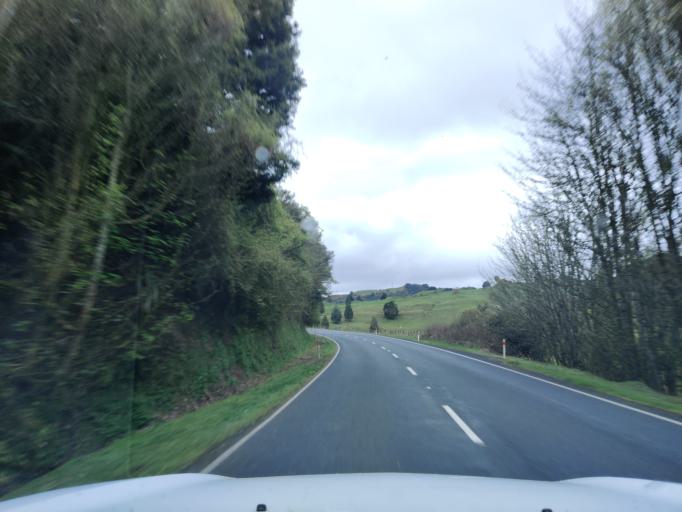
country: NZ
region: Waikato
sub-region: Otorohanga District
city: Otorohanga
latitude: -38.5949
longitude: 175.2194
